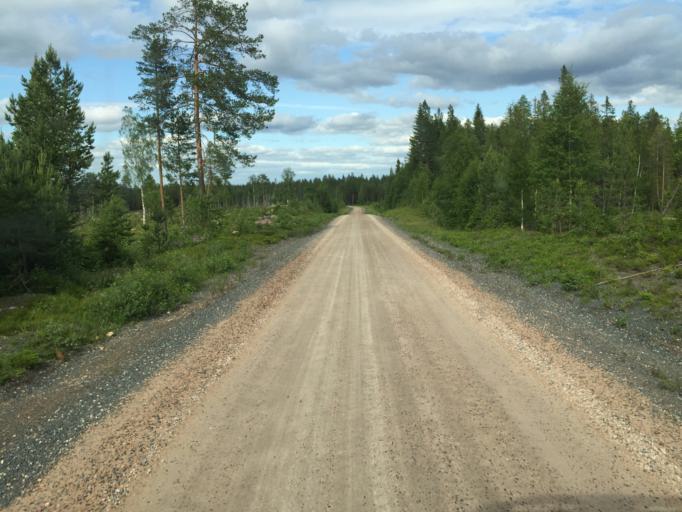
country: SE
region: Dalarna
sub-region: Malung-Saelens kommun
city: Malung
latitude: 60.9198
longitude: 13.7867
